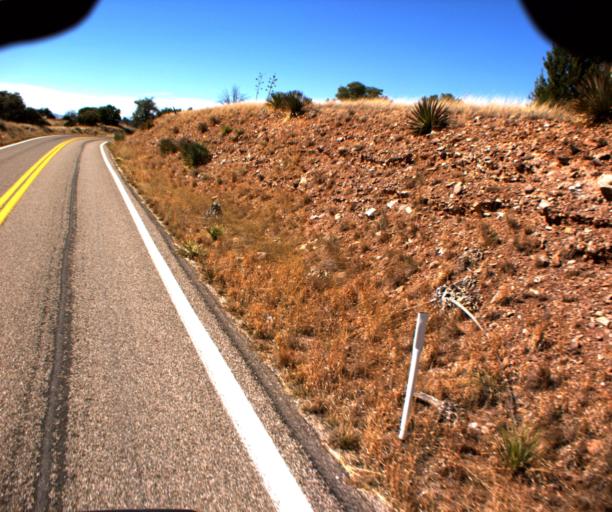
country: US
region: Arizona
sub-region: Cochise County
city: Huachuca City
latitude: 31.5187
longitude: -110.4984
